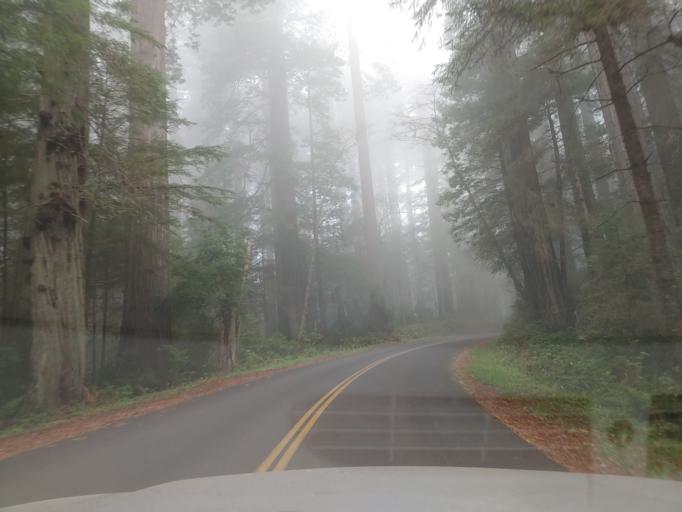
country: US
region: California
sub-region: Del Norte County
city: Bertsch-Oceanview
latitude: 41.4621
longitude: -124.0552
